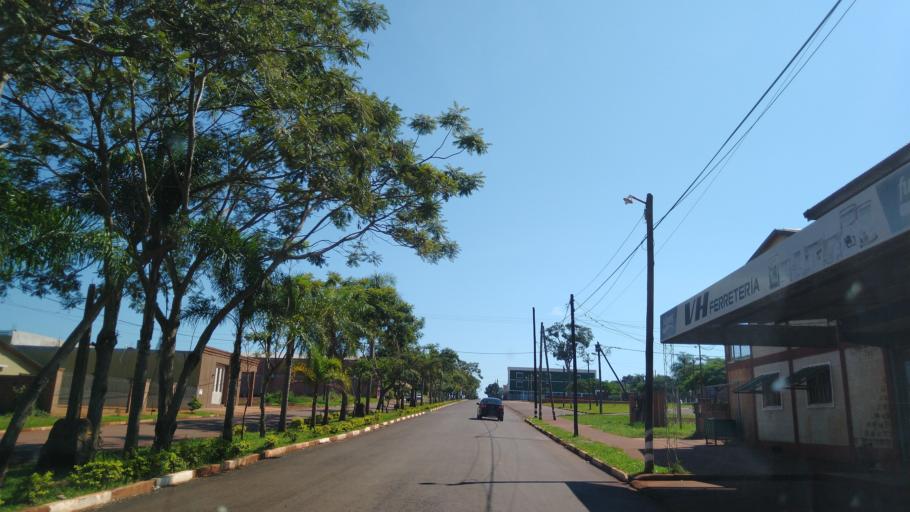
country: AR
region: Misiones
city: Puerto Libertad
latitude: -25.9665
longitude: -54.5605
